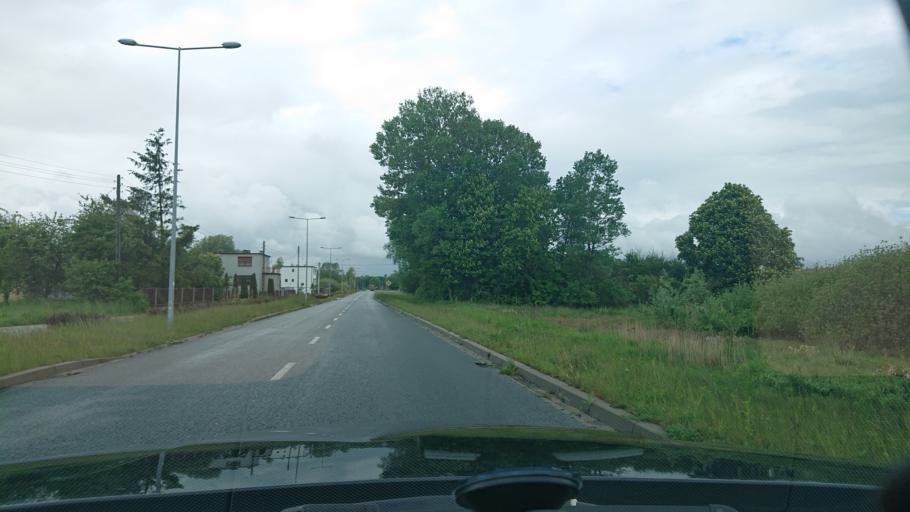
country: PL
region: Greater Poland Voivodeship
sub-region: Powiat gnieznienski
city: Gniezno
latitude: 52.5227
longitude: 17.6214
